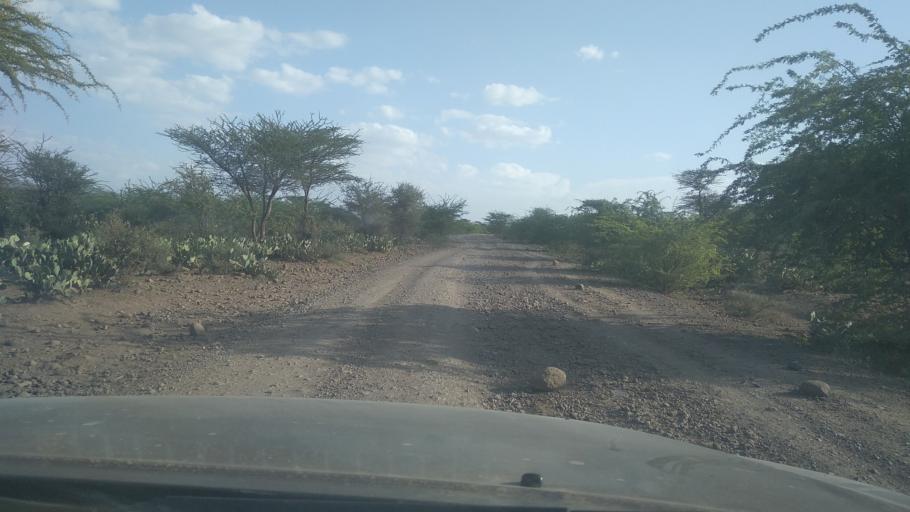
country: ET
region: Oromiya
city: Hirna
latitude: 9.4415
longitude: 40.9859
